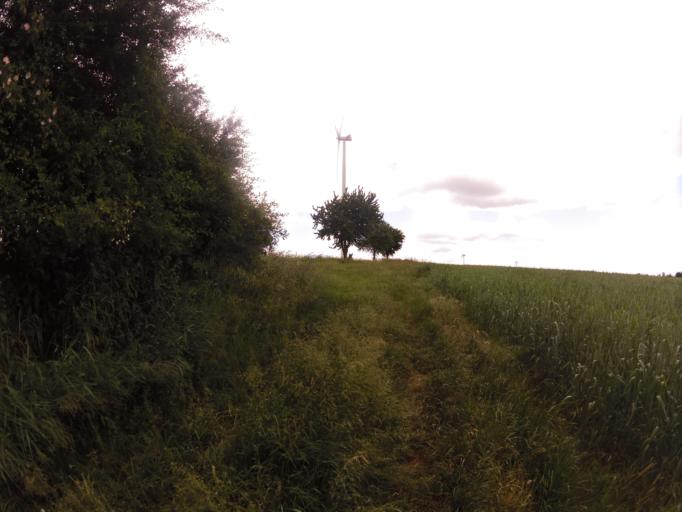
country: DE
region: Bavaria
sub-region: Regierungsbezirk Unterfranken
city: Guntersleben
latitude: 49.8778
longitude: 9.8782
